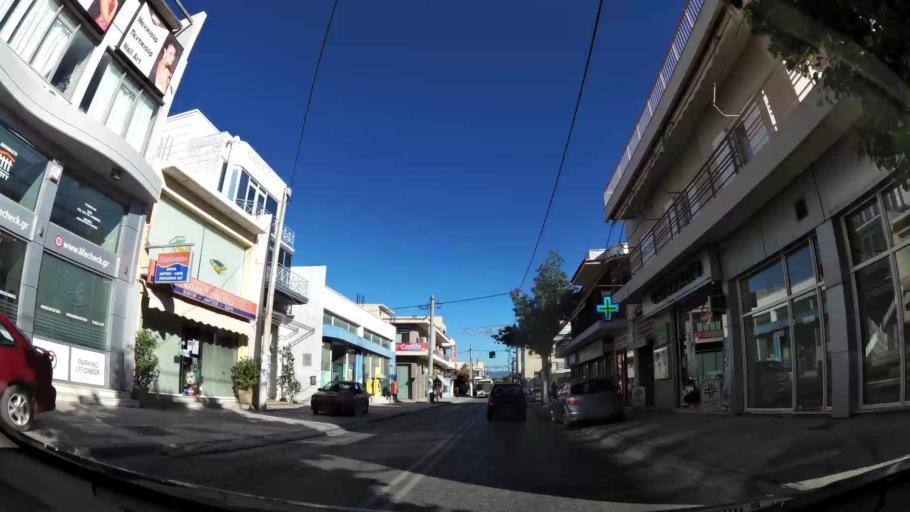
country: GR
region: Attica
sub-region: Nomarchia Anatolikis Attikis
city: Koropi
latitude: 37.9071
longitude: 23.8730
